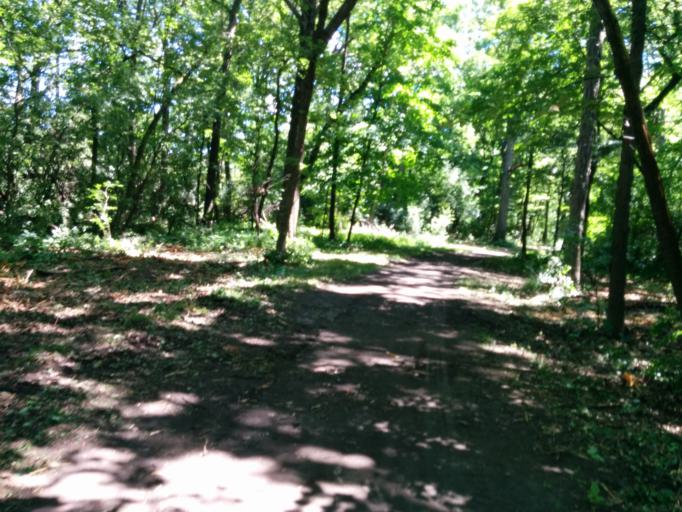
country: US
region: Illinois
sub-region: Cook County
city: Park Ridge
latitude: 41.9982
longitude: -87.8562
